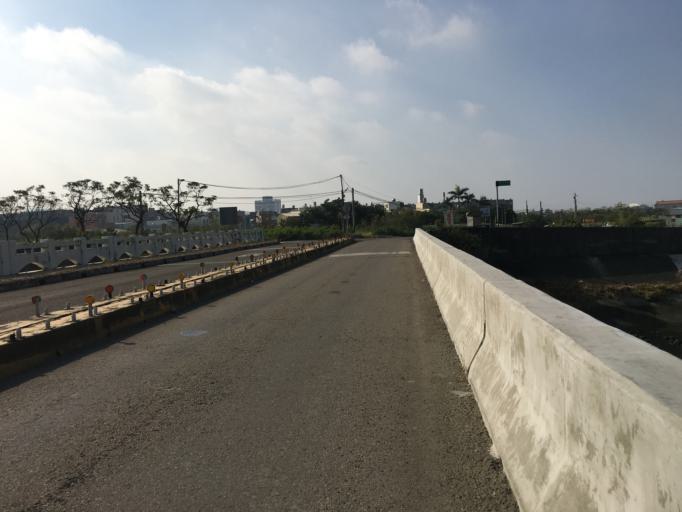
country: TW
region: Taiwan
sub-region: Hsinchu
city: Hsinchu
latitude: 24.8034
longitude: 120.9252
